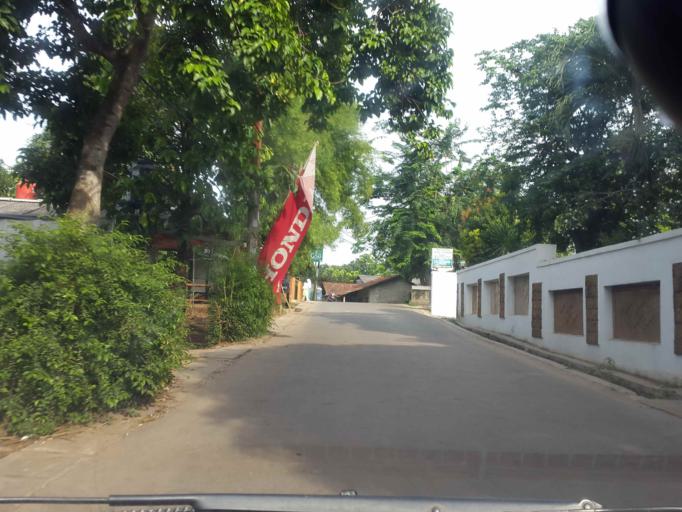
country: ID
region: Banten
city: South Tangerang
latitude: -6.2805
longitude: 106.6800
